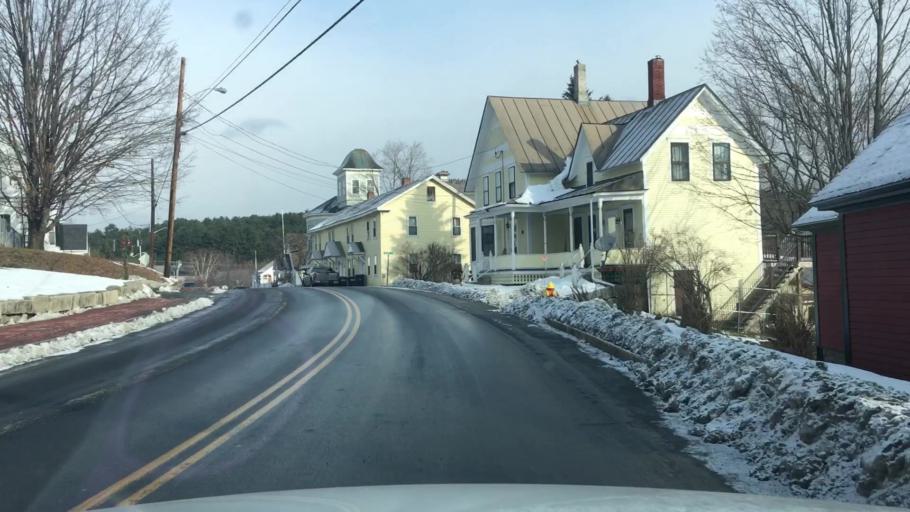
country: US
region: New Hampshire
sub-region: Grafton County
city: Enfield
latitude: 43.6421
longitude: -72.1448
